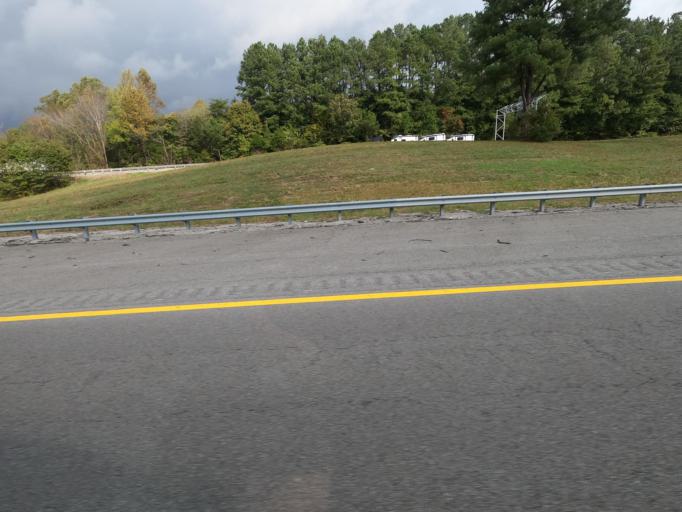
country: US
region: Tennessee
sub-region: Dickson County
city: Burns
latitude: 36.0179
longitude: -87.2531
